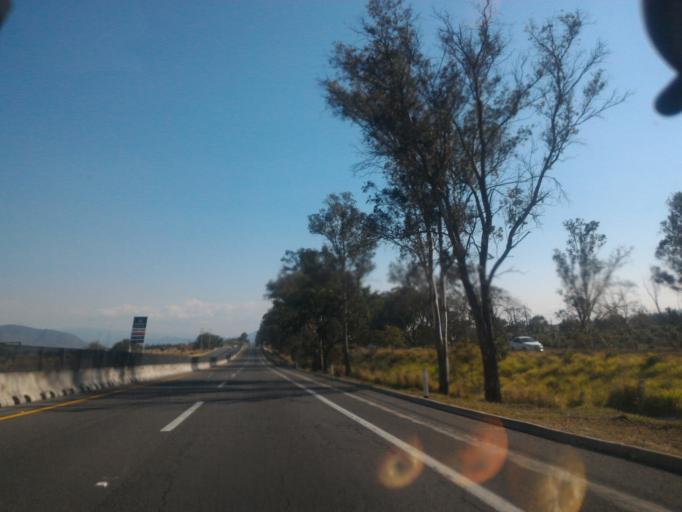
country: MX
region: Jalisco
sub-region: Zapotlan el Grande
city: Ciudad Guzman [CERESO]
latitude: 19.6309
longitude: -103.4659
